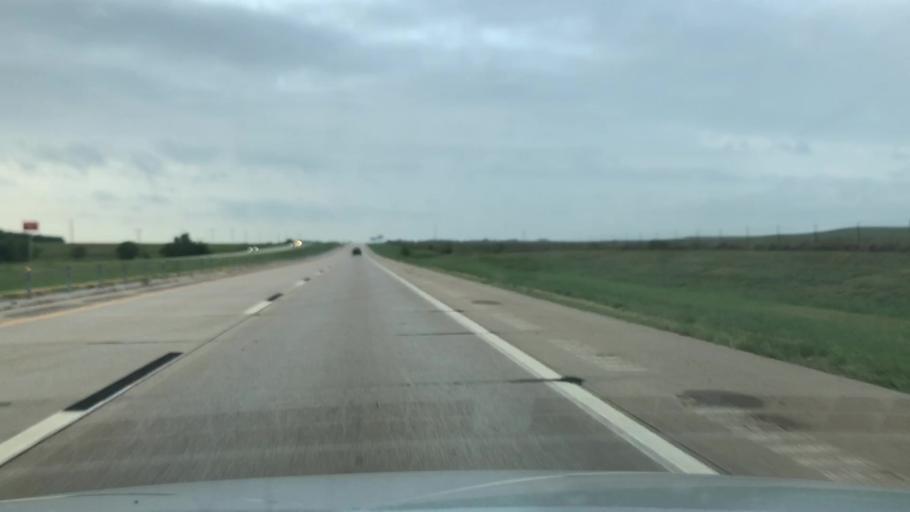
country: US
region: Oklahoma
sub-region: Osage County
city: Skiatook
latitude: 36.3868
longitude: -95.9208
